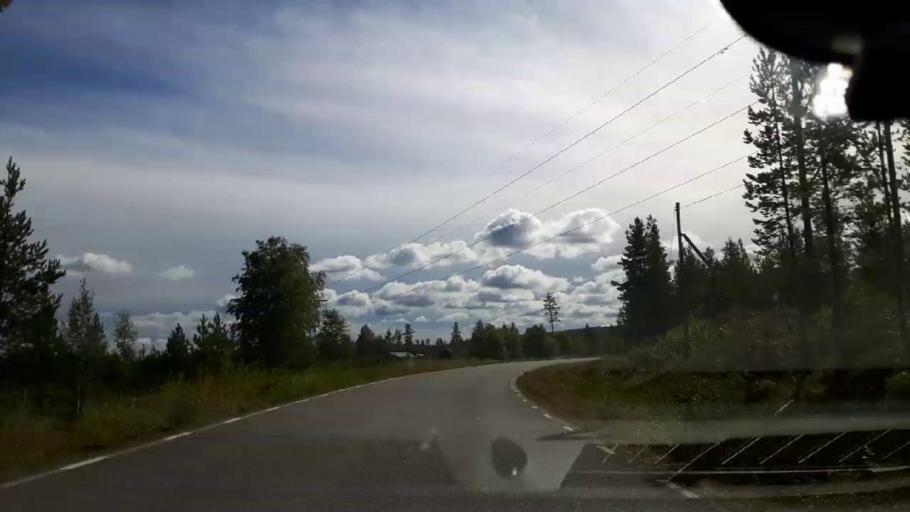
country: SE
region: Jaemtland
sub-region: Braecke Kommun
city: Braecke
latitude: 63.1997
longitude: 15.3672
